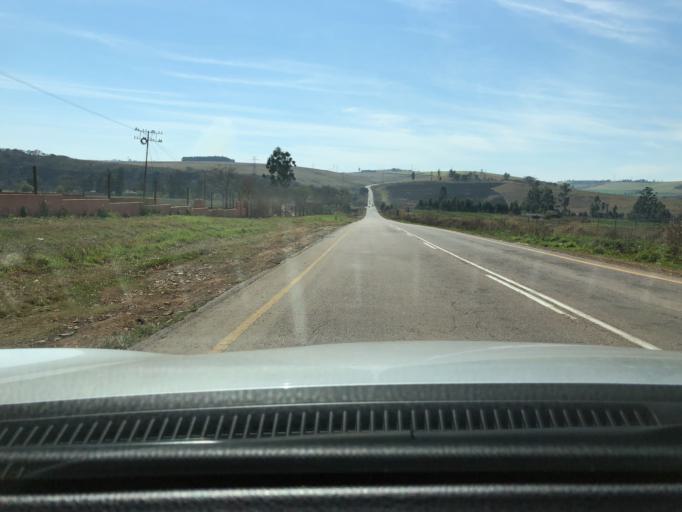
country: ZA
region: KwaZulu-Natal
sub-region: uMgungundlovu District Municipality
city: Richmond
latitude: -29.7760
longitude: 30.3576
